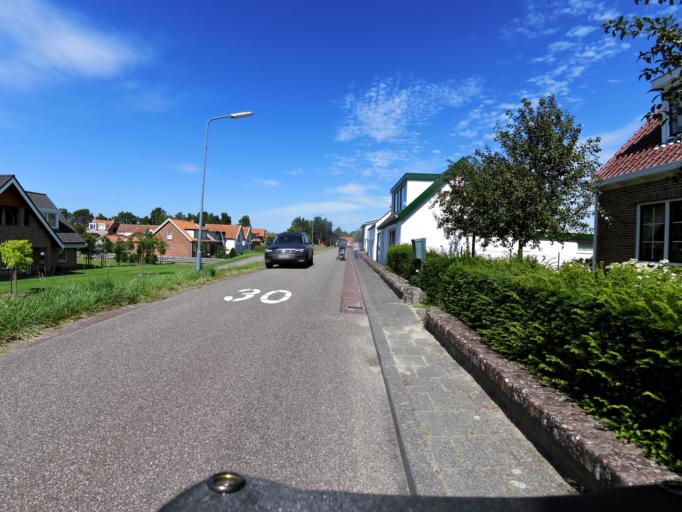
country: NL
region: Zeeland
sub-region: Gemeente Noord-Beveland
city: Kamperland
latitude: 51.5663
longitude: 3.6983
